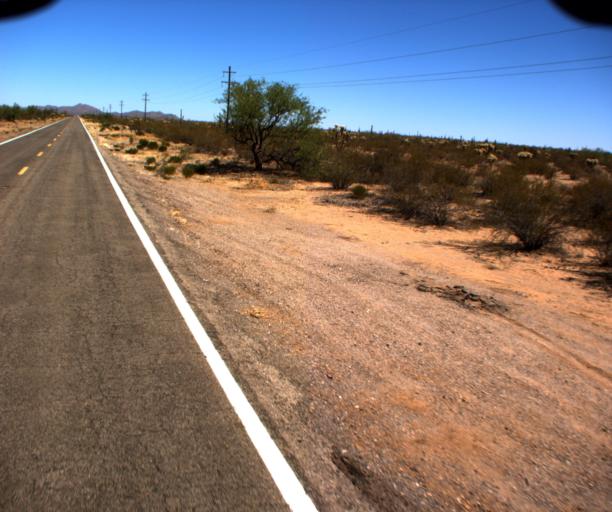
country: US
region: Arizona
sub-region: Pima County
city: Sells
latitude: 32.0948
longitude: -112.0613
